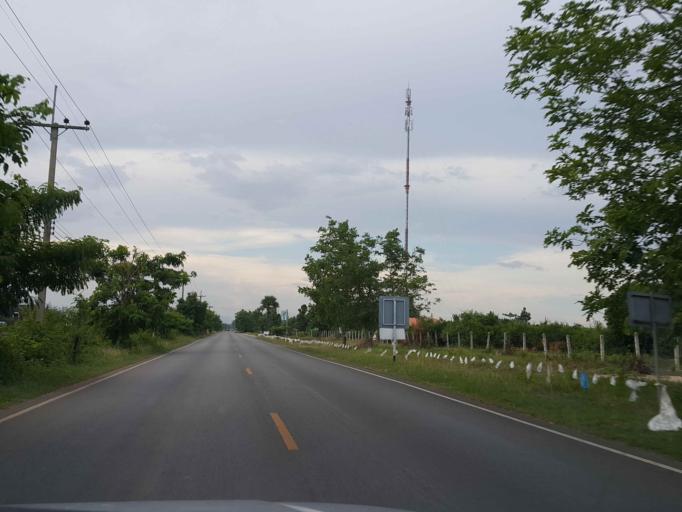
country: TH
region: Lampang
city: Ko Kha
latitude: 18.2341
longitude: 99.3898
